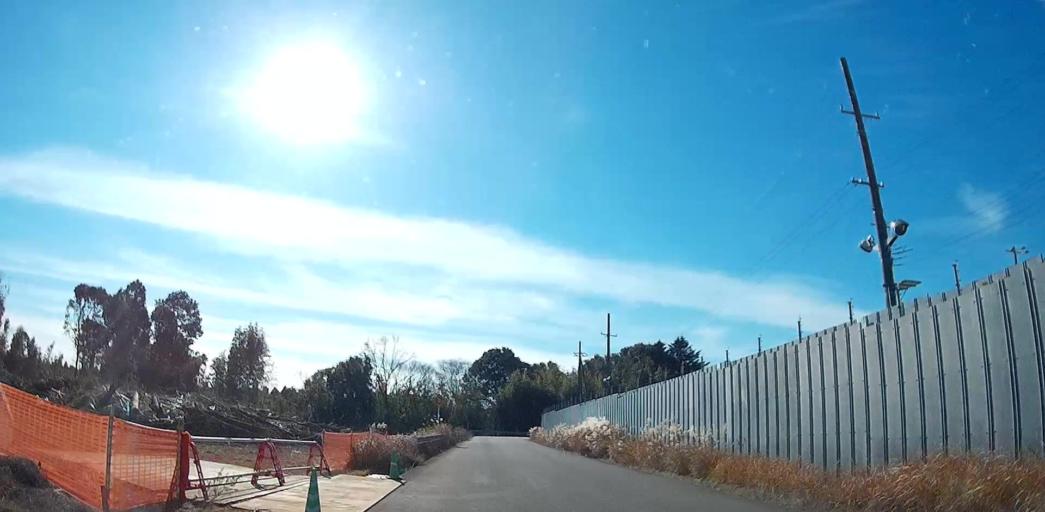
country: JP
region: Chiba
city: Narita
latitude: 35.7653
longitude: 140.4021
